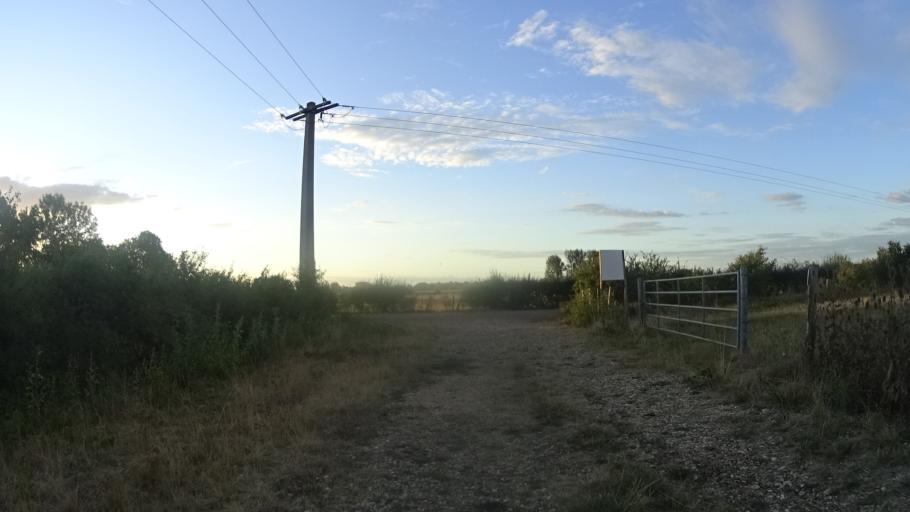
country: FR
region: Bourgogne
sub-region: Departement de la Cote-d'Or
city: Seurre
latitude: 46.9870
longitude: 5.1239
